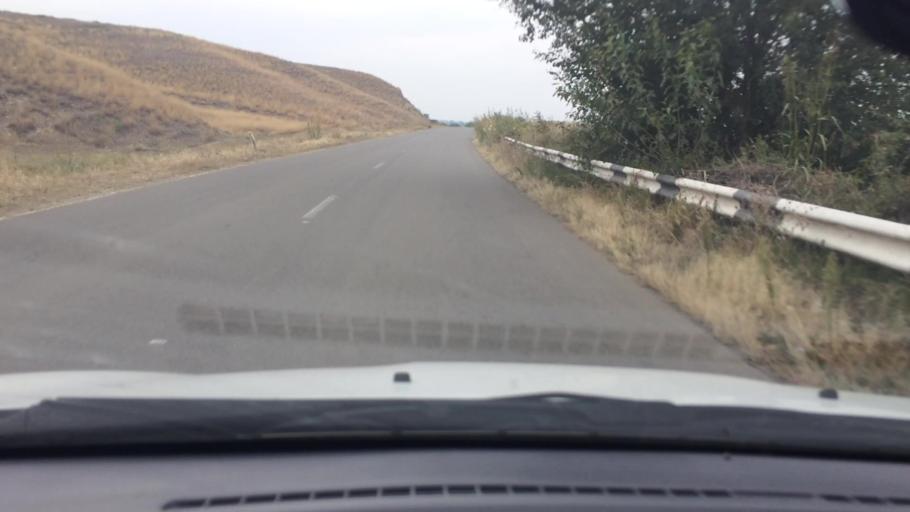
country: AM
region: Tavush
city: Berdavan
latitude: 41.3399
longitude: 44.9966
